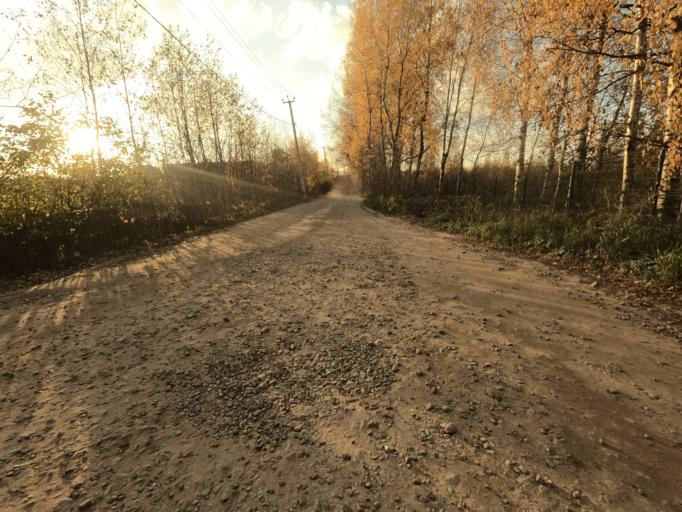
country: RU
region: St.-Petersburg
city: Beloostrov
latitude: 60.1789
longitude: 30.0388
